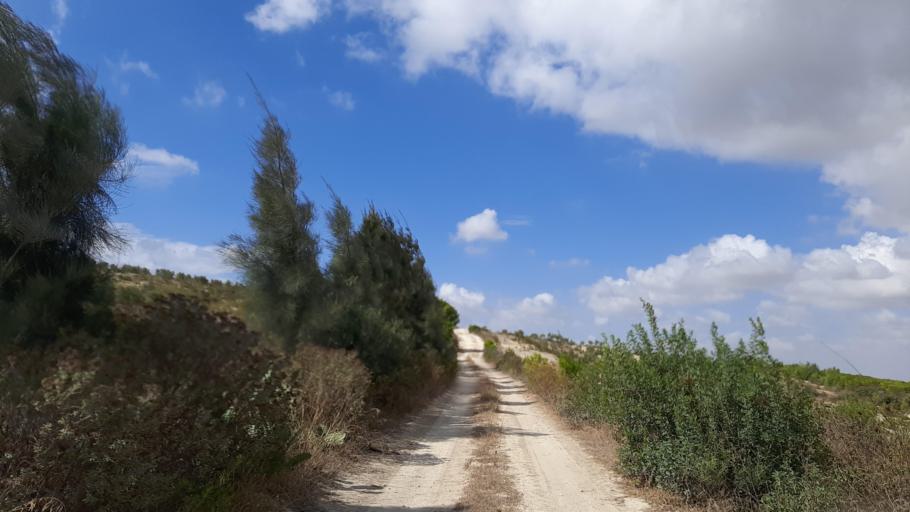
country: TN
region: Zaghwan
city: Zaghouan
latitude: 36.4989
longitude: 10.1756
